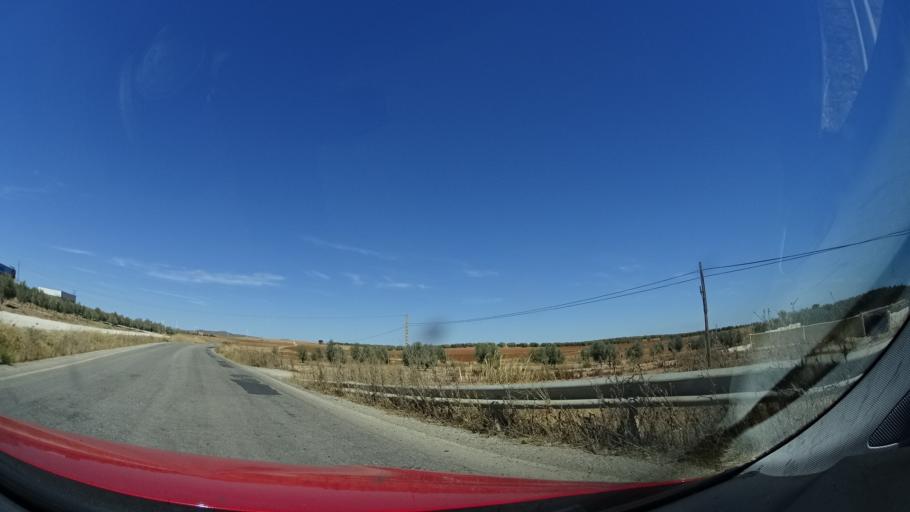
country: ES
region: Andalusia
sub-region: Provincia de Malaga
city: Campillos
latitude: 37.0674
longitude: -4.8608
